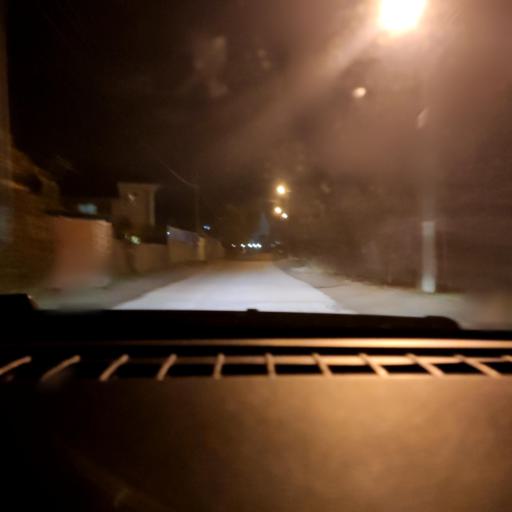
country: RU
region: Voronezj
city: Somovo
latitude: 51.6792
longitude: 39.3299
